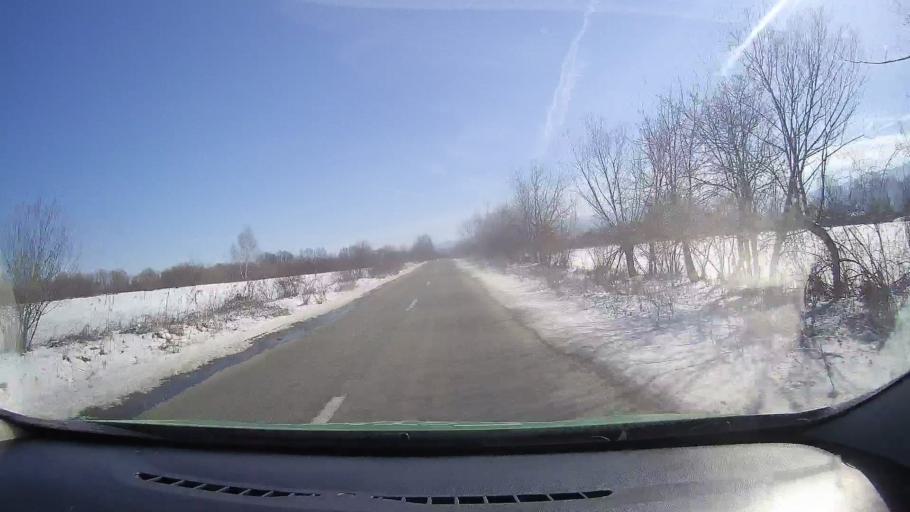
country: RO
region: Brasov
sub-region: Comuna Harseni
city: Harseni
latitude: 45.7322
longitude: 25.0191
